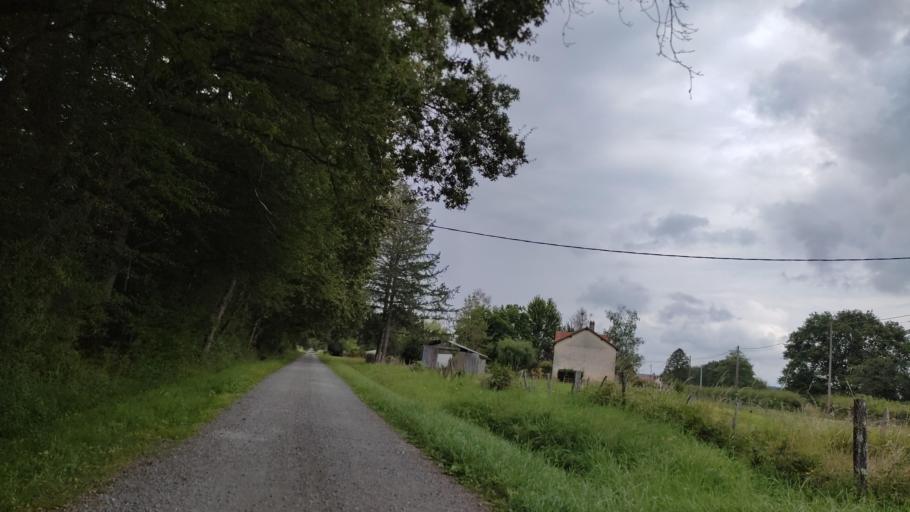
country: FR
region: Bourgogne
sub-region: Departement de la Nievre
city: Cercy-la-Tour
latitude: 46.7938
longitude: 3.6159
